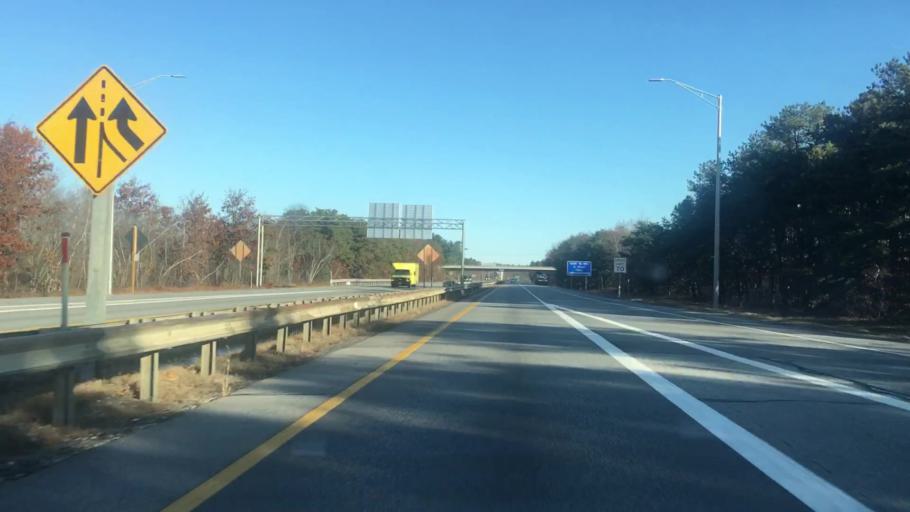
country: US
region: Maine
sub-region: Cumberland County
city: New Gloucester
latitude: 43.9381
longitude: -70.3345
